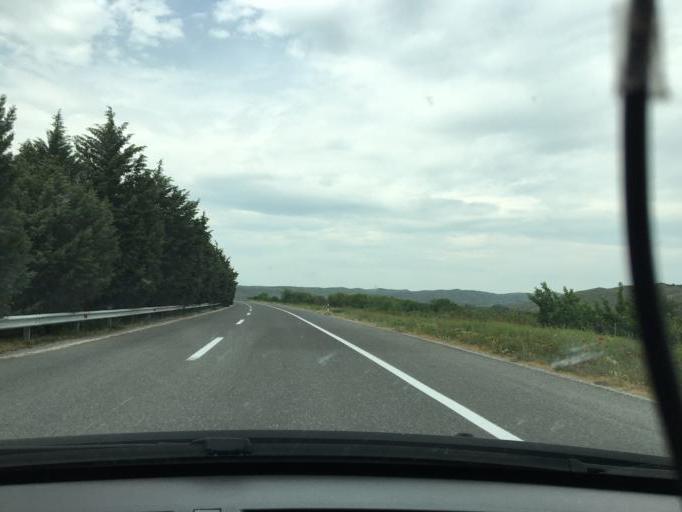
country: MK
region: Gradsko
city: Gradsko
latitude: 41.5556
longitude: 22.0209
